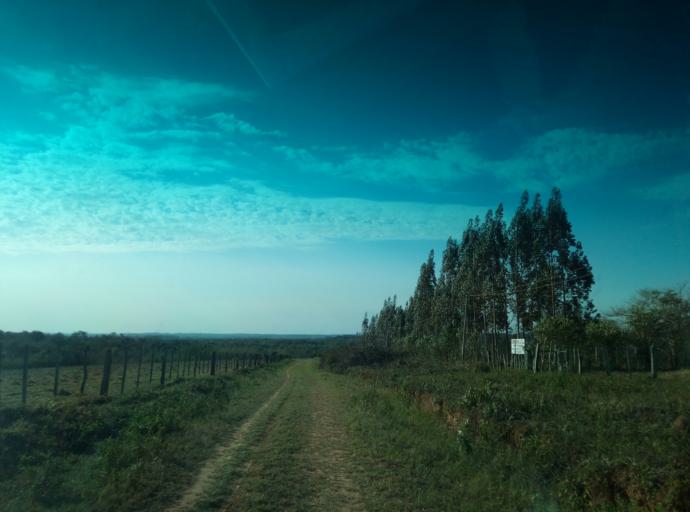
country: PY
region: Caaguazu
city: Doctor Cecilio Baez
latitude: -25.1612
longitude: -56.2320
